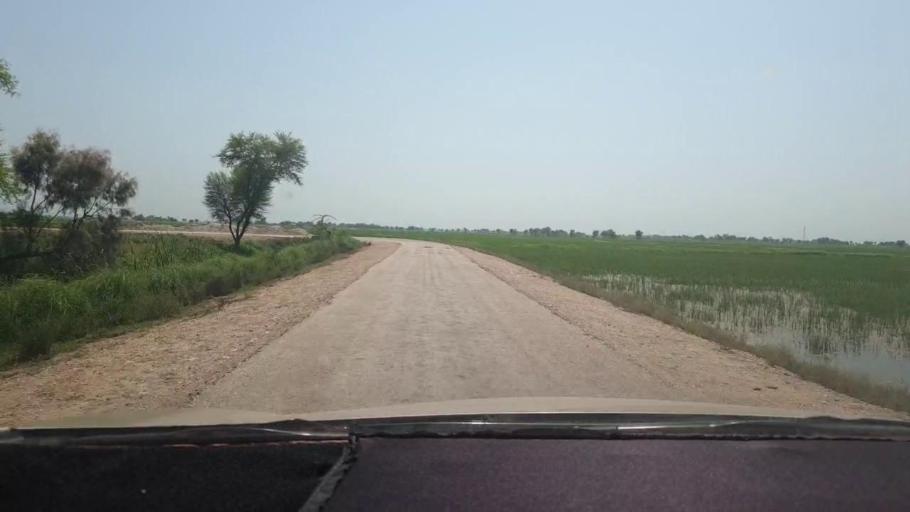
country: PK
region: Sindh
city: Miro Khan
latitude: 27.6752
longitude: 68.0942
